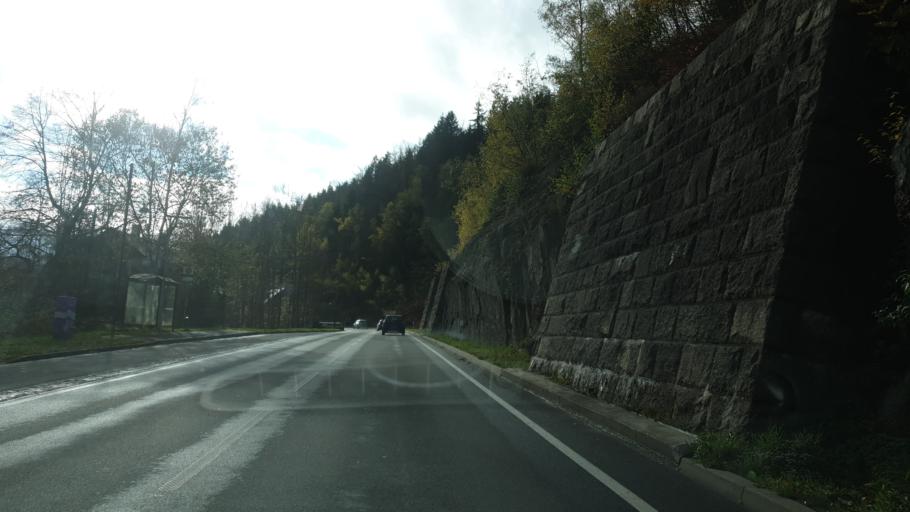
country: DE
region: Saxony
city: Zschorlau
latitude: 50.5421
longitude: 12.6572
